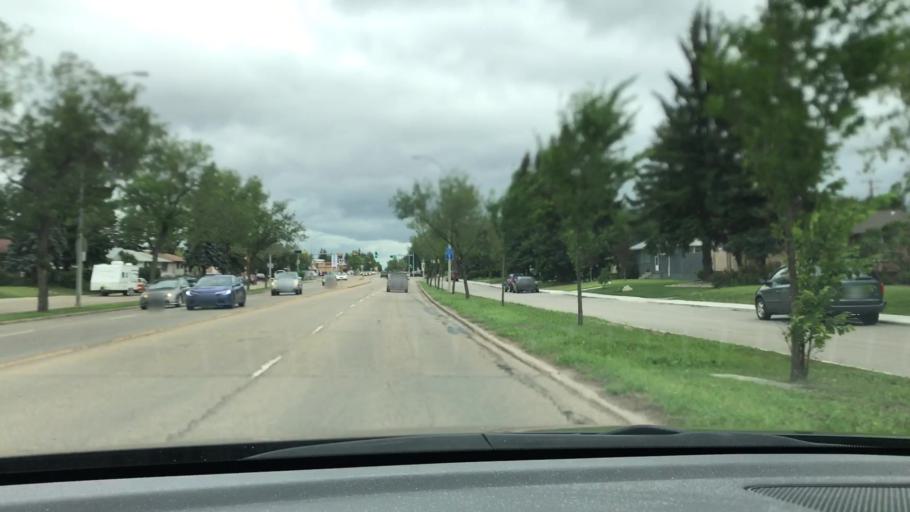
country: CA
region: Alberta
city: Edmonton
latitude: 53.5173
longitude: -113.5778
